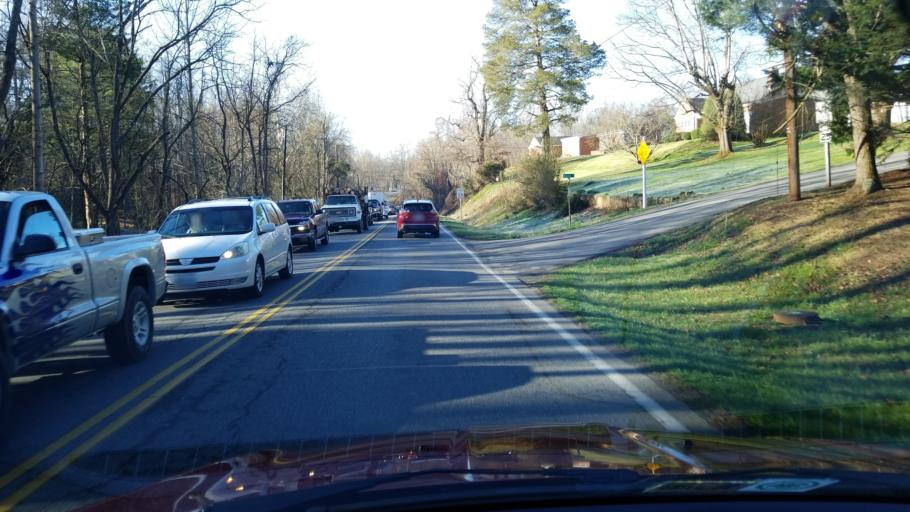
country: US
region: Virginia
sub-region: Franklin County
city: Rocky Mount
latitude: 36.9950
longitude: -79.8939
